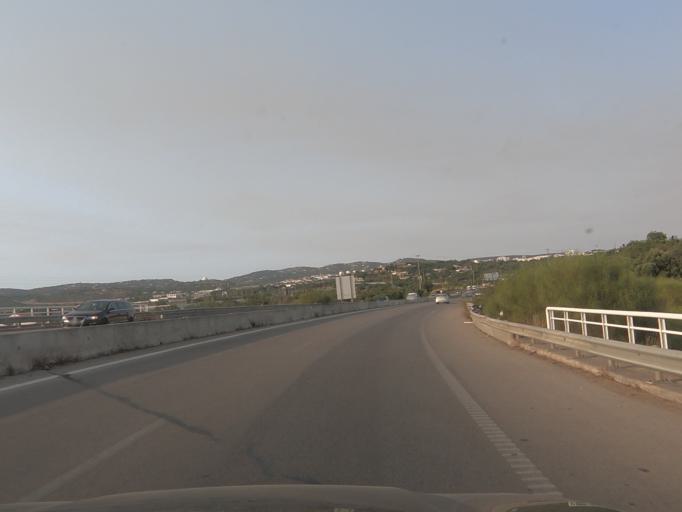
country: PT
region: Faro
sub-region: Loule
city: Almancil
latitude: 37.1133
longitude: -8.0449
